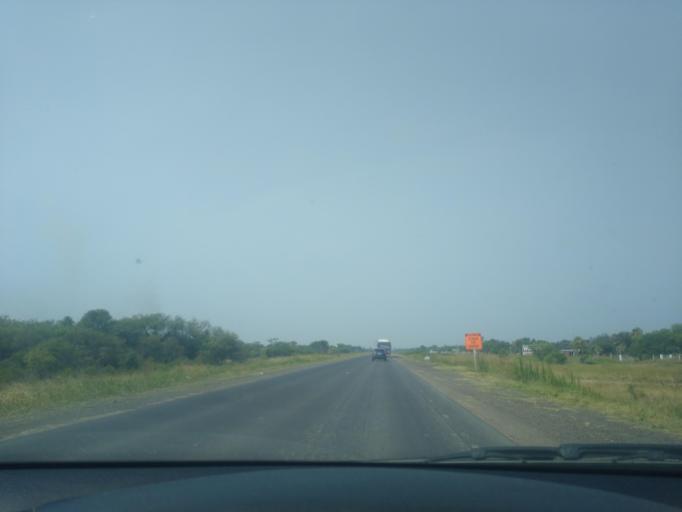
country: AR
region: Chaco
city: Fontana
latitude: -27.4866
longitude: -59.0688
